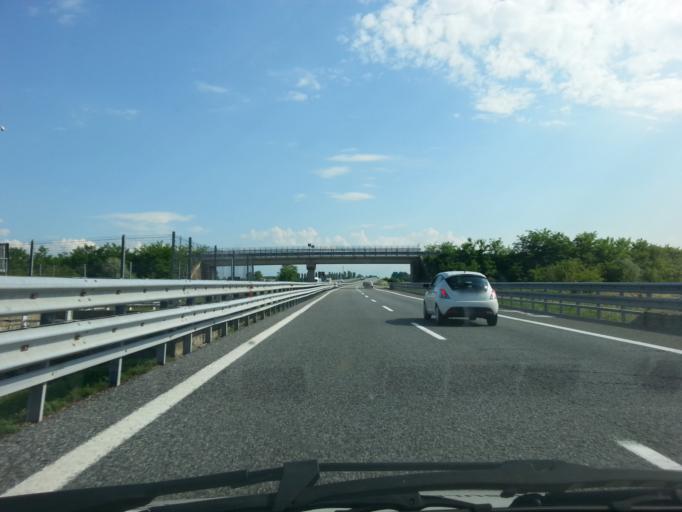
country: IT
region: Piedmont
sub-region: Provincia di Cuneo
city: Caramagna Piemonte
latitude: 44.7893
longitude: 7.7530
